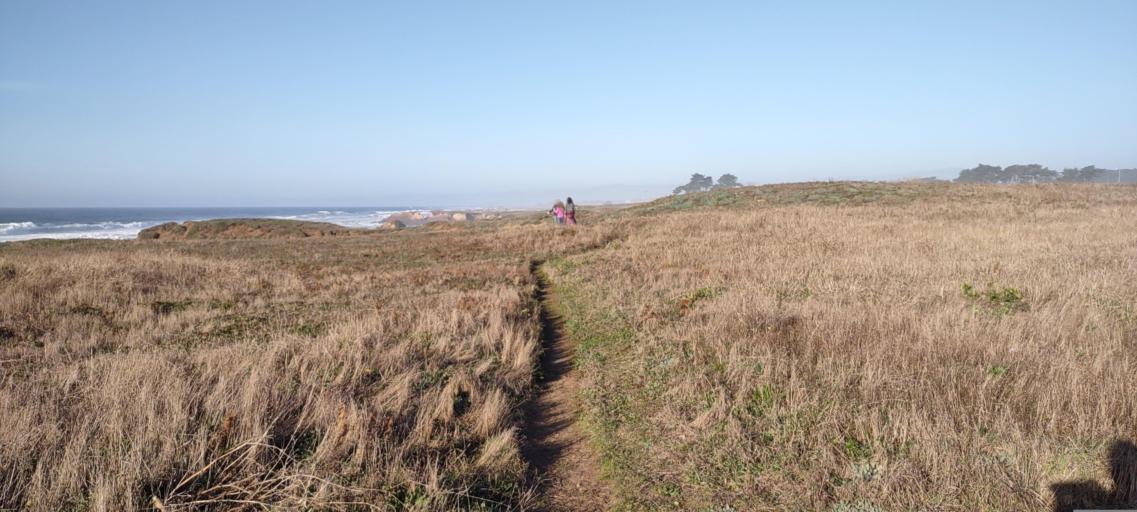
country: US
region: California
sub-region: Mendocino County
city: Fort Bragg
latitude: 39.4554
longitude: -123.8104
